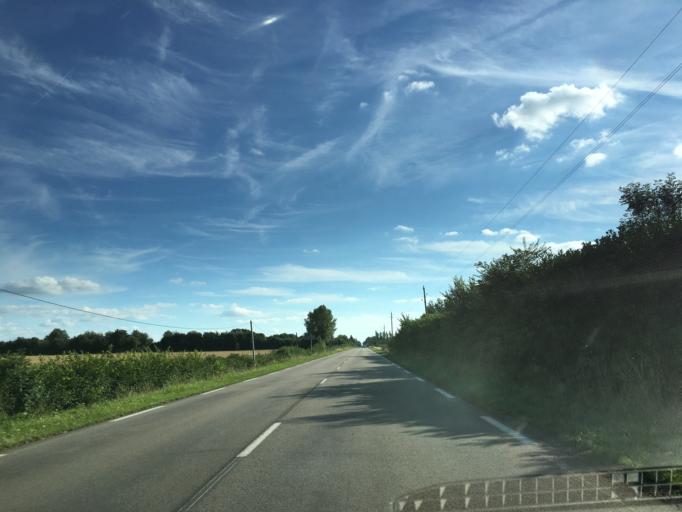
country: FR
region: Lower Normandy
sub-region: Departement du Calvados
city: Orbec
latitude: 48.9176
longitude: 0.4264
